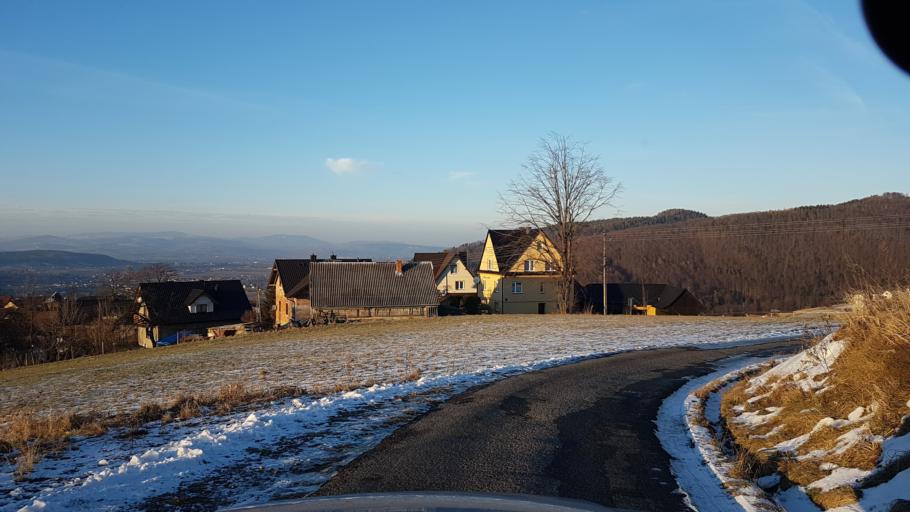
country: PL
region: Lesser Poland Voivodeship
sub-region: Powiat nowosadecki
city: Rytro
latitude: 49.5102
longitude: 20.6716
